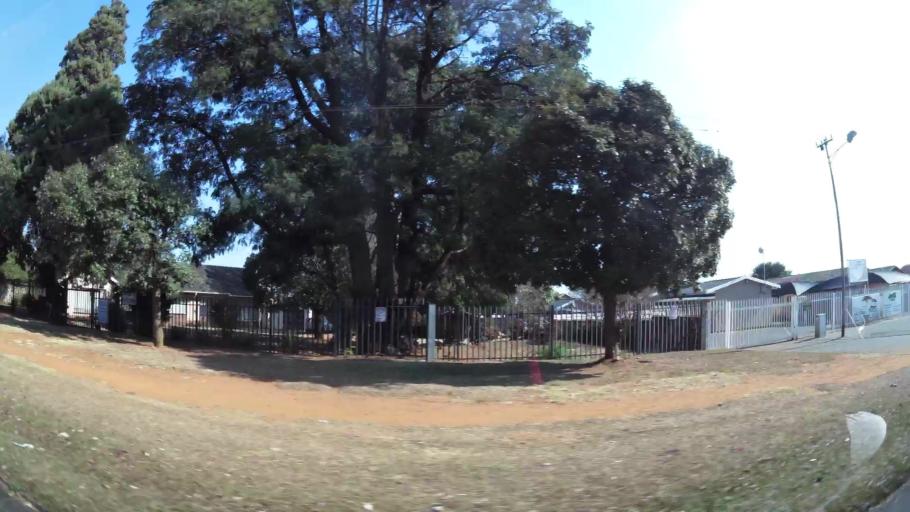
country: ZA
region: Gauteng
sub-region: West Rand District Municipality
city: Randfontein
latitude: -26.1652
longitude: 27.6963
